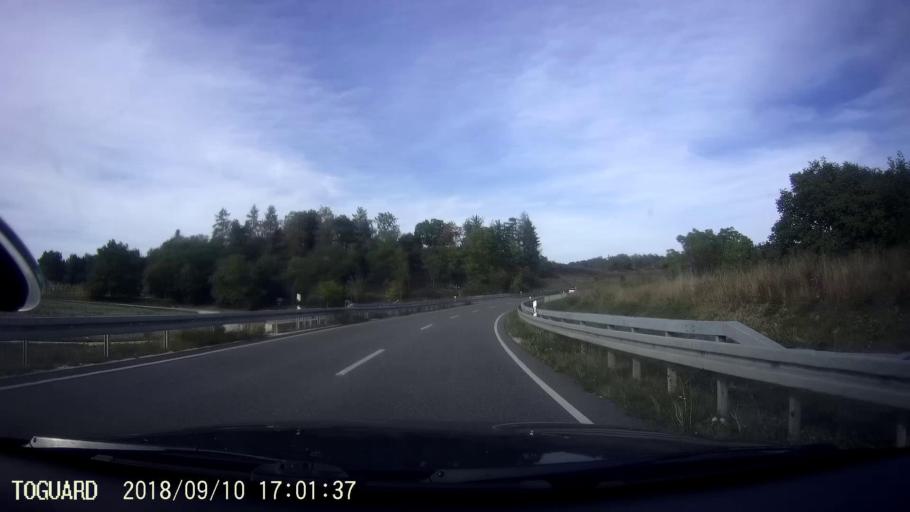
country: CH
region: Thurgau
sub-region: Kreuzlingen District
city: Gottlieben
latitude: 47.6964
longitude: 9.1330
